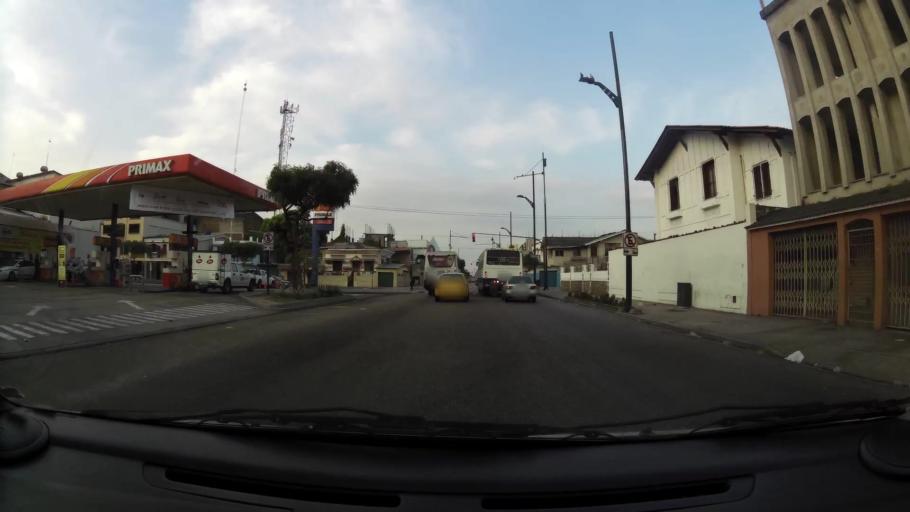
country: EC
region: Guayas
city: Guayaquil
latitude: -2.1898
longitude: -79.8946
